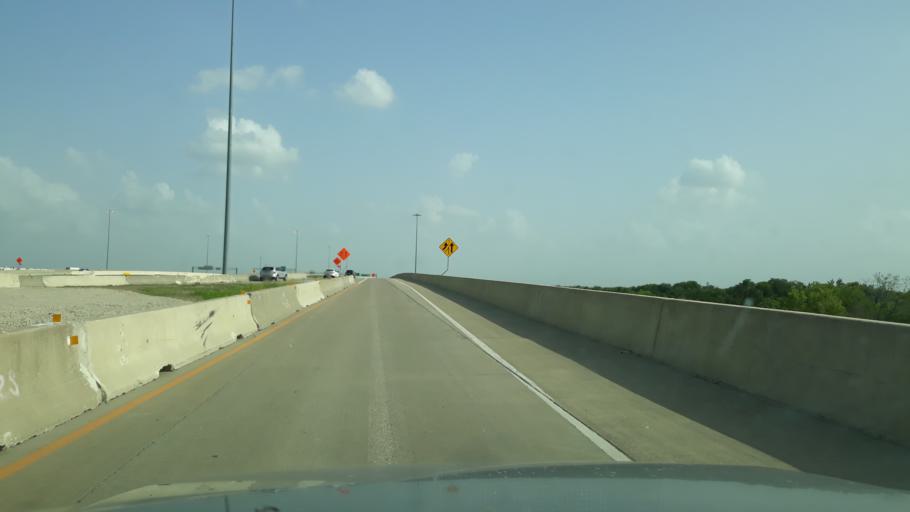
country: US
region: Texas
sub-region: Dallas County
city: Coppell
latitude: 32.9480
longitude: -97.0417
